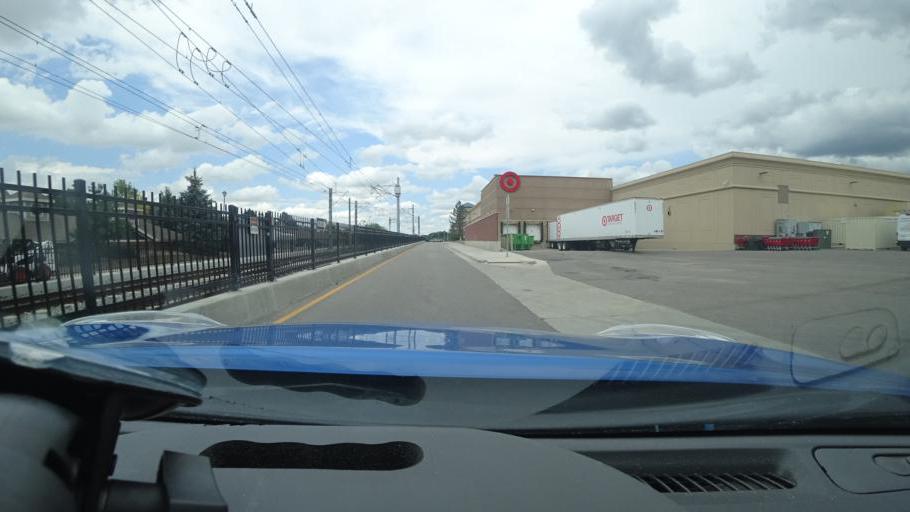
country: US
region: Colorado
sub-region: Adams County
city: Aurora
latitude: 39.7165
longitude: -104.8230
